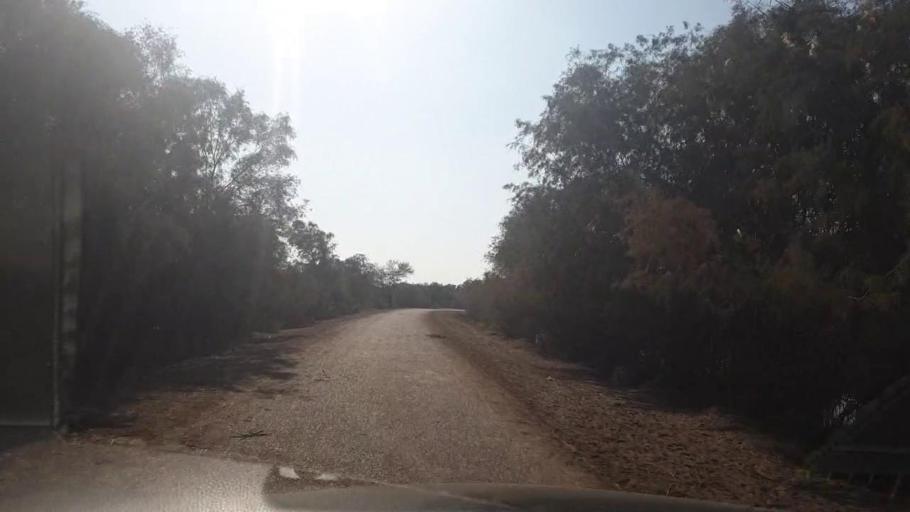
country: PK
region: Sindh
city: Khairpur
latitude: 28.1387
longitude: 69.6010
